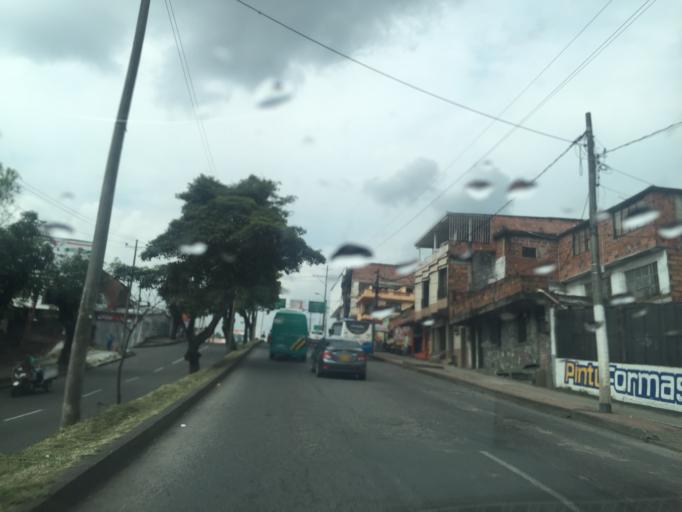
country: CO
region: Risaralda
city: Pereira
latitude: 4.8048
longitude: -75.6936
